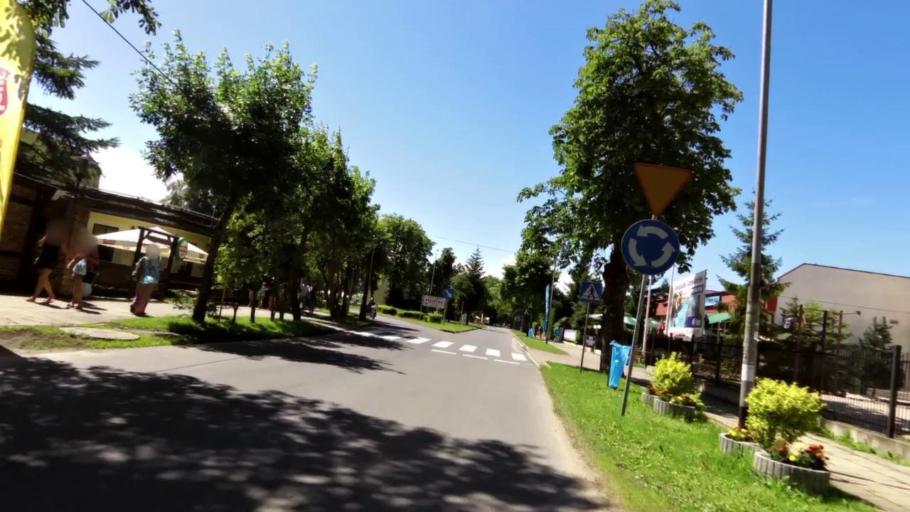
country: PL
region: West Pomeranian Voivodeship
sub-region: Koszalin
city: Koszalin
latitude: 54.3078
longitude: 16.1968
